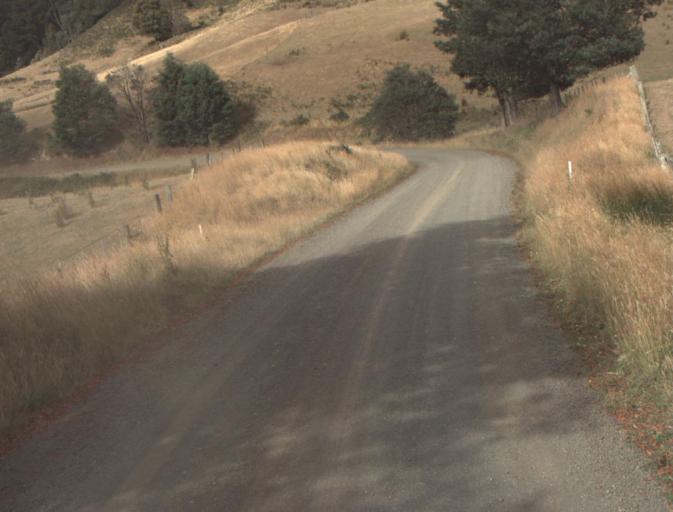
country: AU
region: Tasmania
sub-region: Dorset
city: Scottsdale
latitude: -41.4459
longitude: 147.5870
